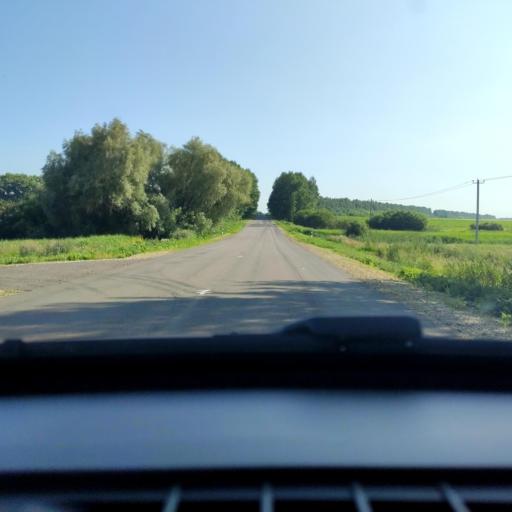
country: RU
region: Voronezj
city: Anna
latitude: 51.6380
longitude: 40.3598
